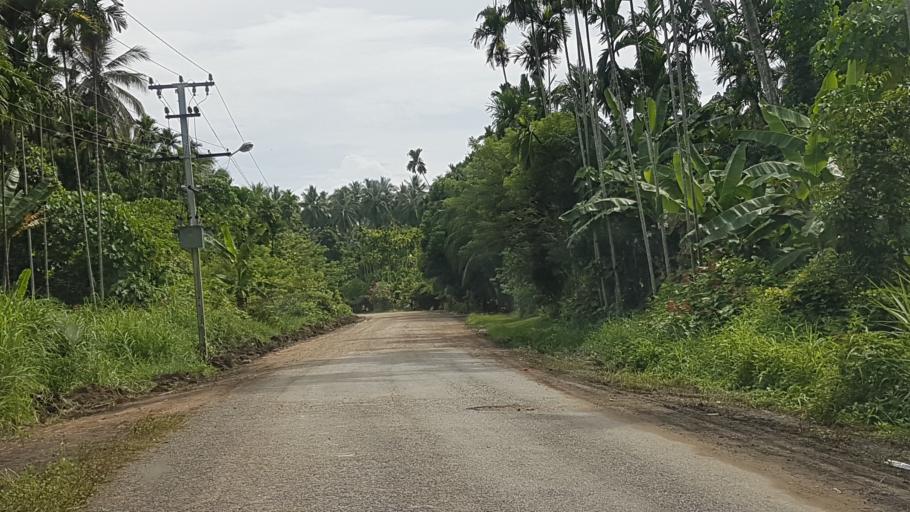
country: PG
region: Madang
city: Madang
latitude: -4.8775
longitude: 145.7950
